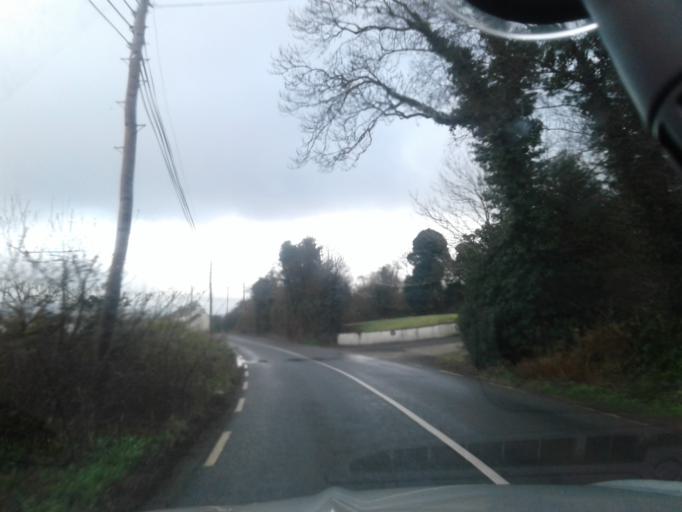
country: IE
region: Ulster
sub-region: County Donegal
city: Ramelton
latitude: 55.0853
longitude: -7.5755
